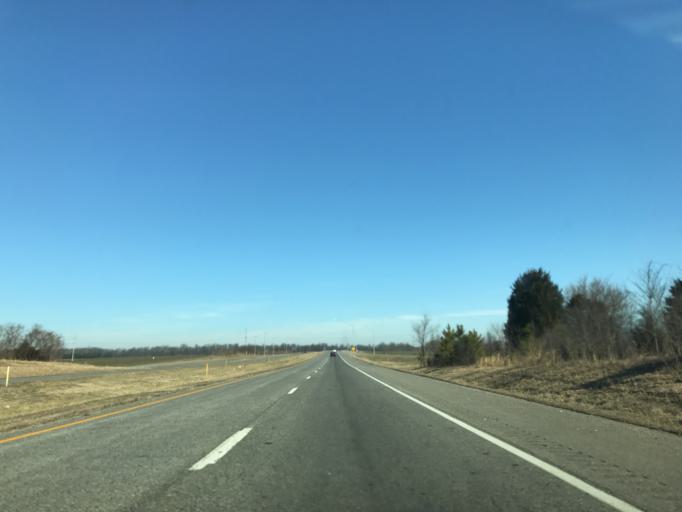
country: US
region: Delaware
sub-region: New Castle County
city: Townsend
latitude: 39.3655
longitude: -75.8153
